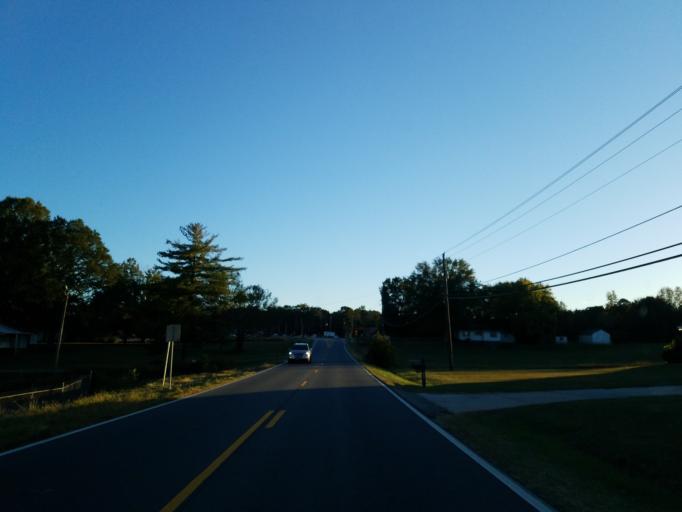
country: US
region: Georgia
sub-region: Forsyth County
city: Cumming
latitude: 34.2641
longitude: -84.1043
